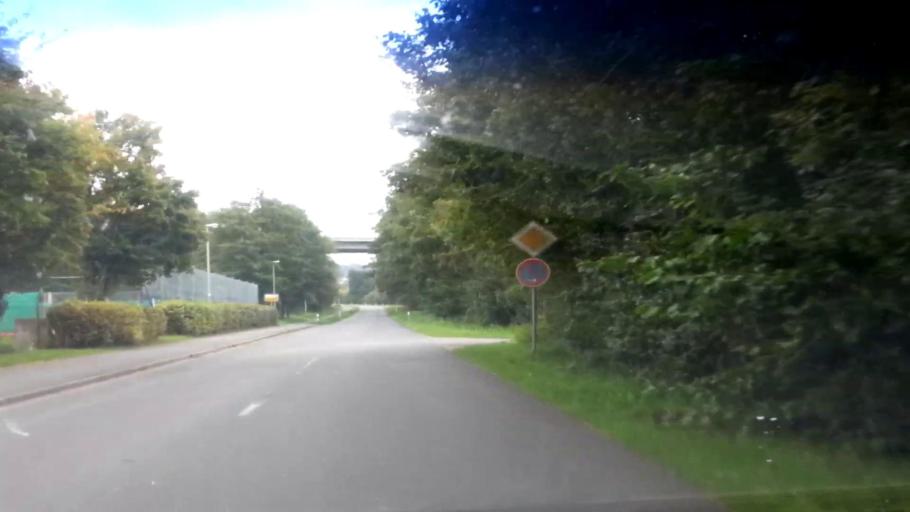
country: DE
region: Bavaria
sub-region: Upper Franconia
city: Zapfendorf
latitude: 50.0103
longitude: 10.9343
